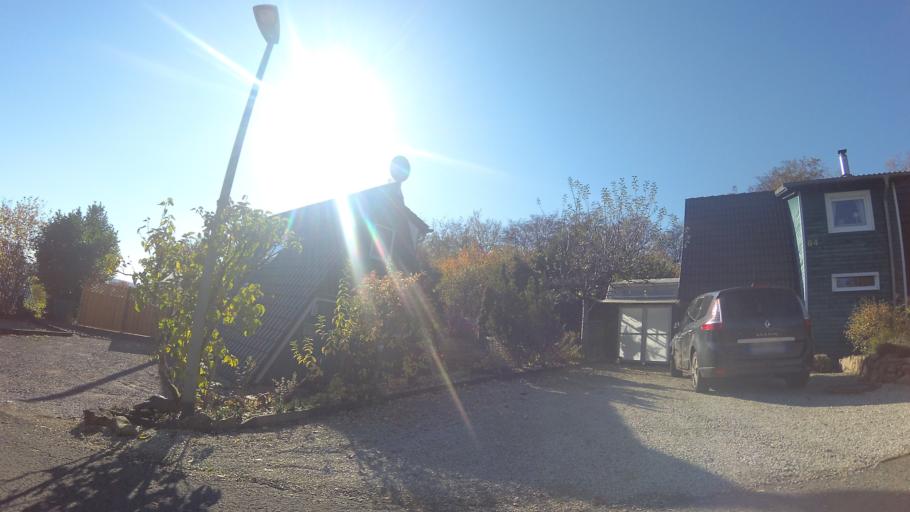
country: DE
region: Saarland
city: Losheim
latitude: 49.5423
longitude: 6.7729
